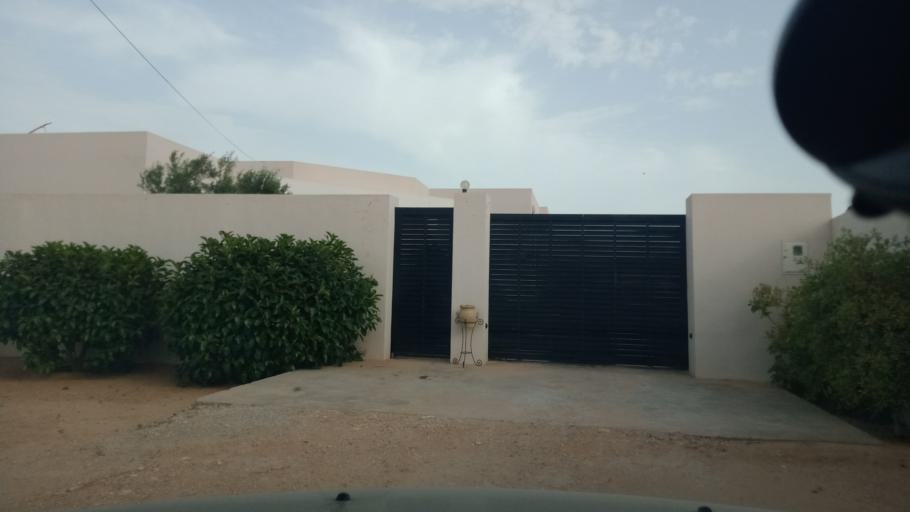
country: TN
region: Safaqis
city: Al Qarmadah
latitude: 34.7853
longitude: 10.7645
